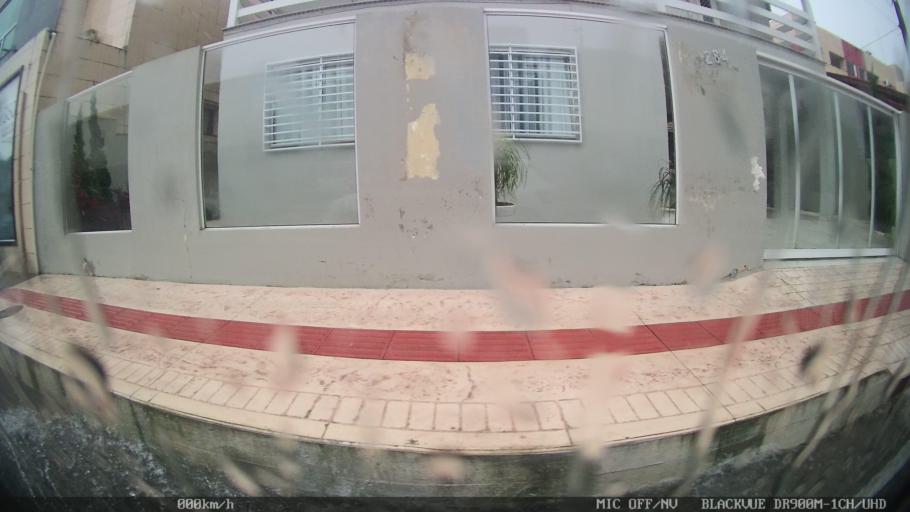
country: BR
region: Santa Catarina
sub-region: Balneario Camboriu
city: Balneario Camboriu
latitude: -26.9739
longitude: -48.6419
